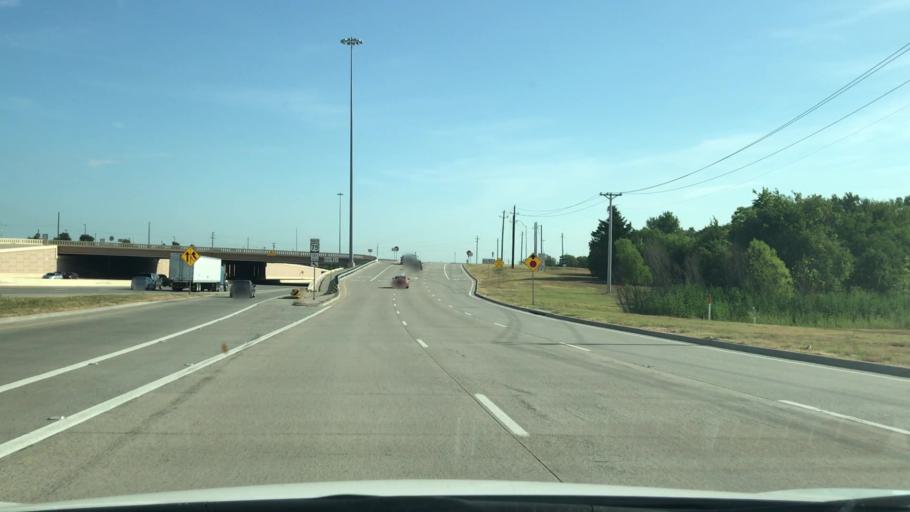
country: US
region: Texas
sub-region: Collin County
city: McKinney
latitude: 33.2377
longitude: -96.6303
